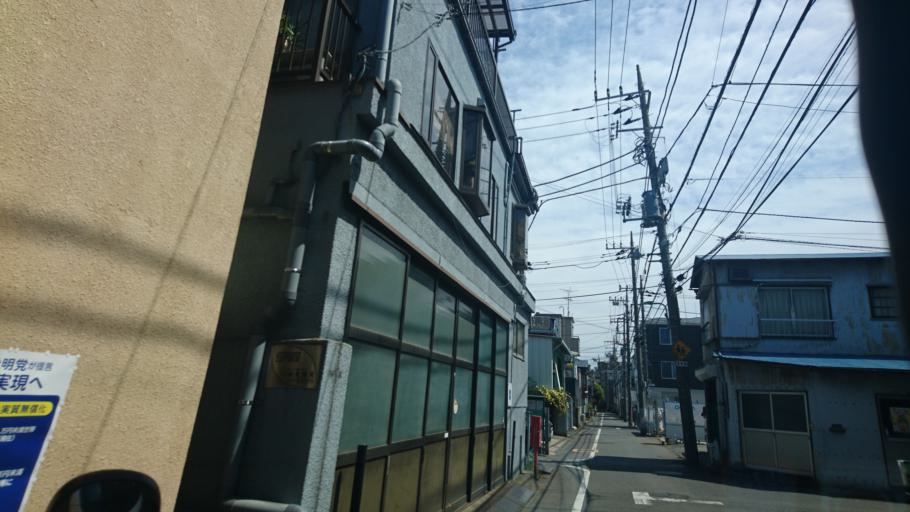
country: JP
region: Kanagawa
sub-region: Kawasaki-shi
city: Kawasaki
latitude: 35.5491
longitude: 139.7195
